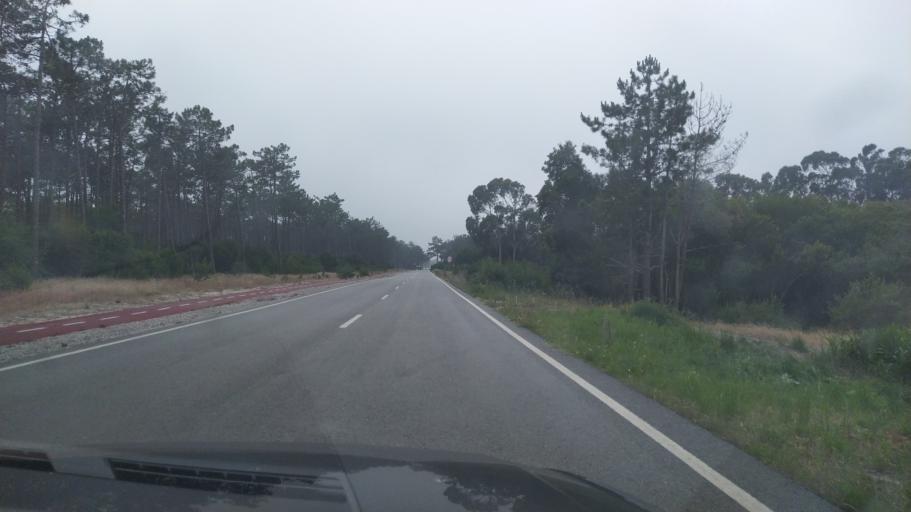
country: PT
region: Aveiro
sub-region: Ilhavo
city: Gafanha da Encarnacao
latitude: 40.5640
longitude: -8.7416
